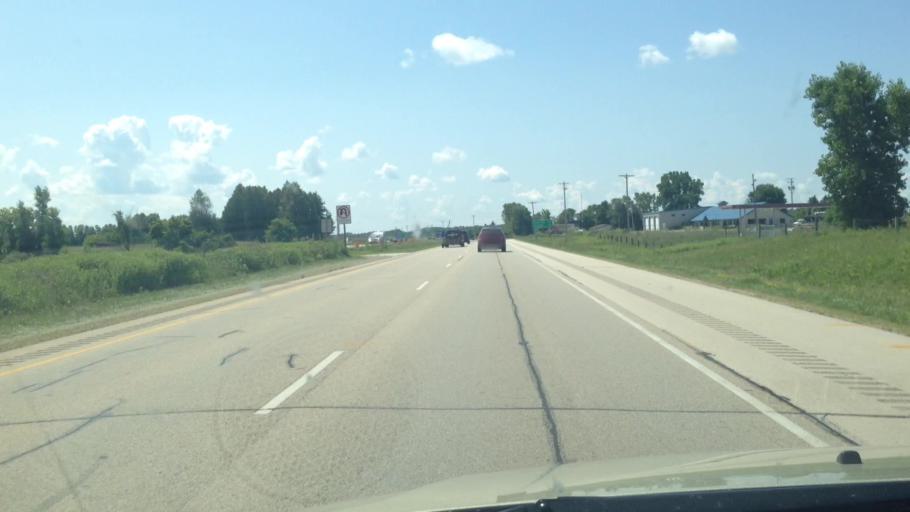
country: US
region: Wisconsin
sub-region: Oconto County
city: Oconto Falls
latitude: 44.7767
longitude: -88.0497
